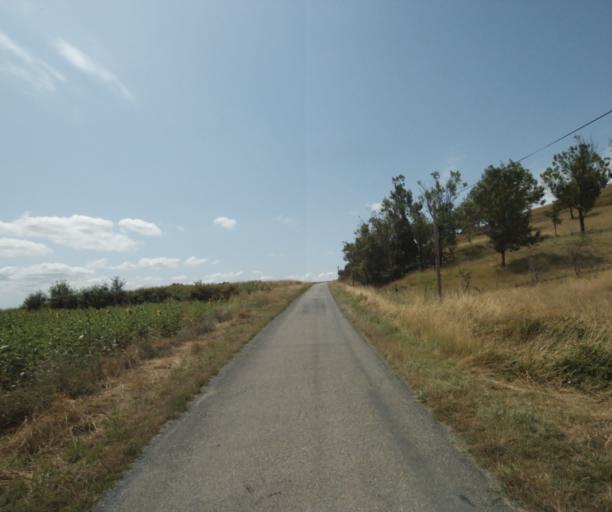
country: FR
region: Midi-Pyrenees
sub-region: Departement de la Haute-Garonne
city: Saint-Felix-Lauragais
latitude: 43.4387
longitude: 1.8865
